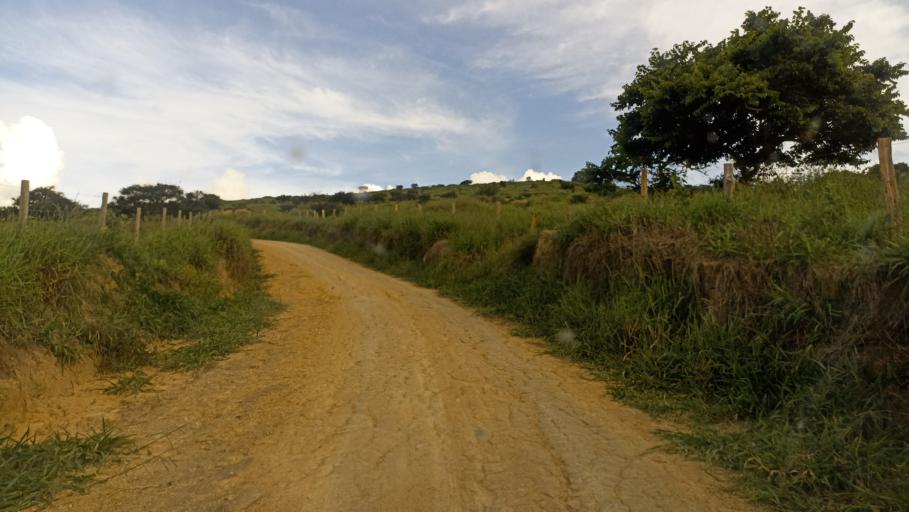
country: BR
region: Minas Gerais
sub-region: Almenara
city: Almenara
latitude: -16.5490
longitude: -40.4574
